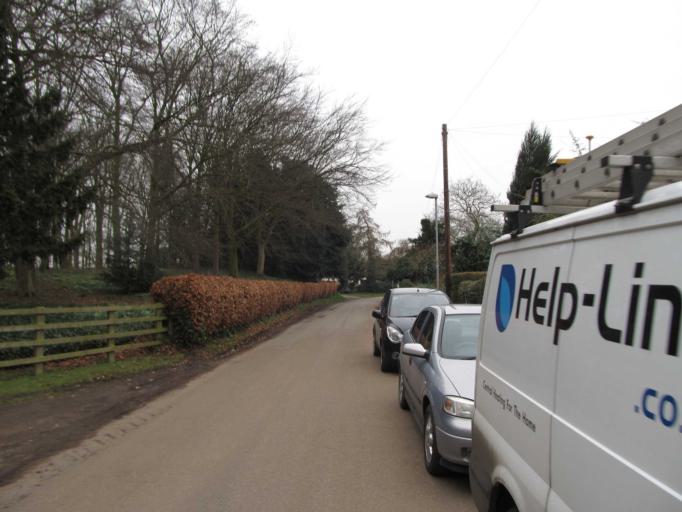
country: GB
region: England
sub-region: Doncaster
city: Bawtry
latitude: 53.4182
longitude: -0.9999
